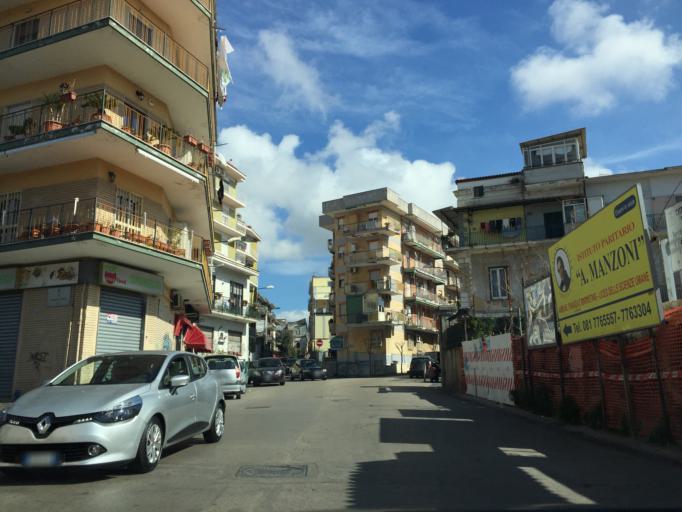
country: IT
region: Campania
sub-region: Provincia di Napoli
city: San Giorgio a Cremano
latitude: 40.8254
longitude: 14.3401
